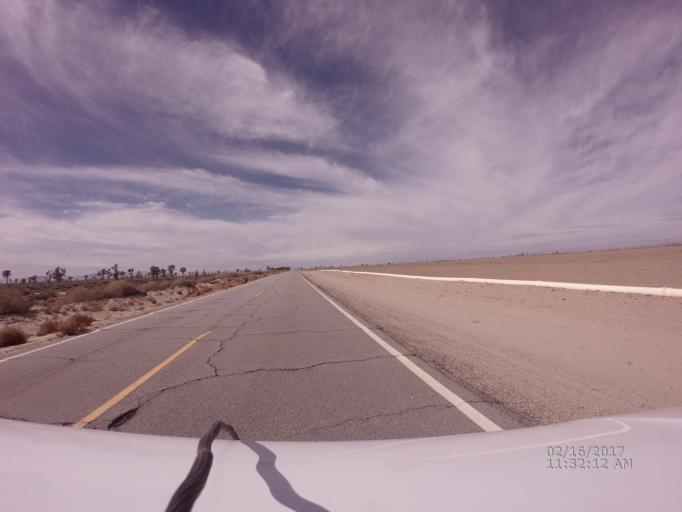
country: US
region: California
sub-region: Los Angeles County
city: Lake Los Angeles
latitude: 34.7047
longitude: -117.9460
